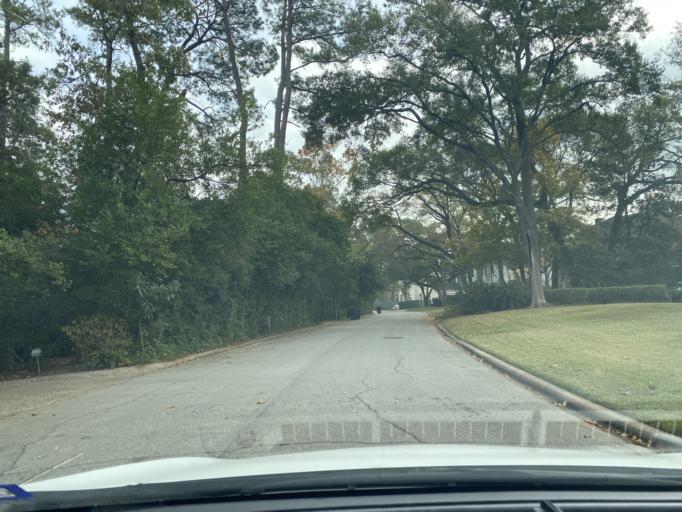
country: US
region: Texas
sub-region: Harris County
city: Hunters Creek Village
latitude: 29.7652
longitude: -95.4617
